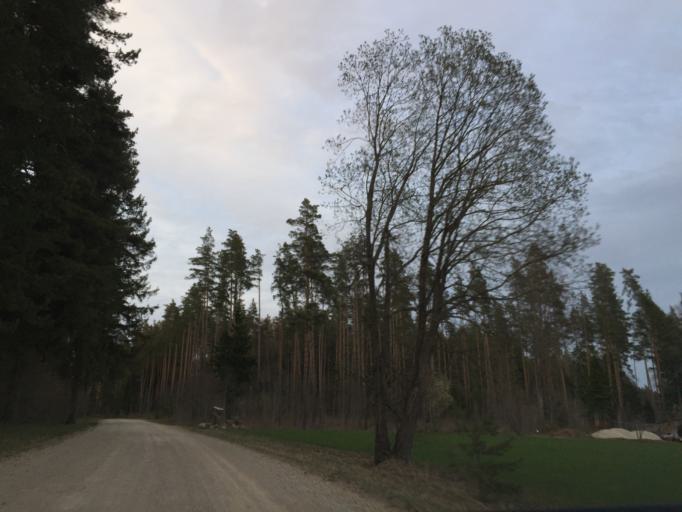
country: EE
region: Tartu
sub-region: UElenurme vald
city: Ulenurme
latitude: 58.2250
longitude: 26.6850
